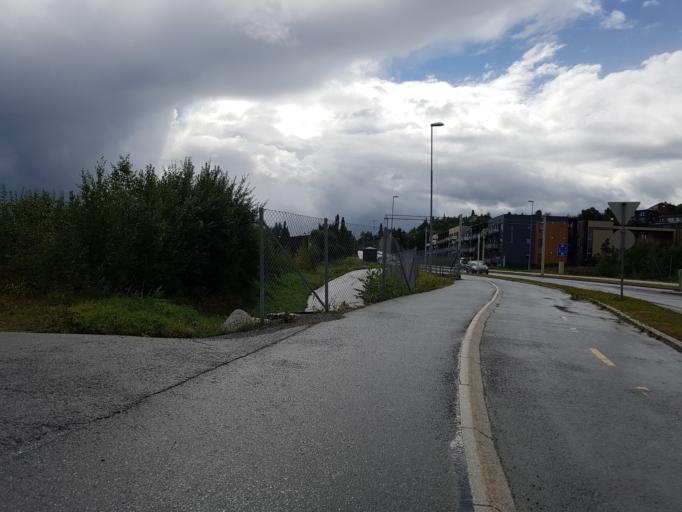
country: NO
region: Sor-Trondelag
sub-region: Trondheim
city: Trondheim
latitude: 63.4059
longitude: 10.3594
